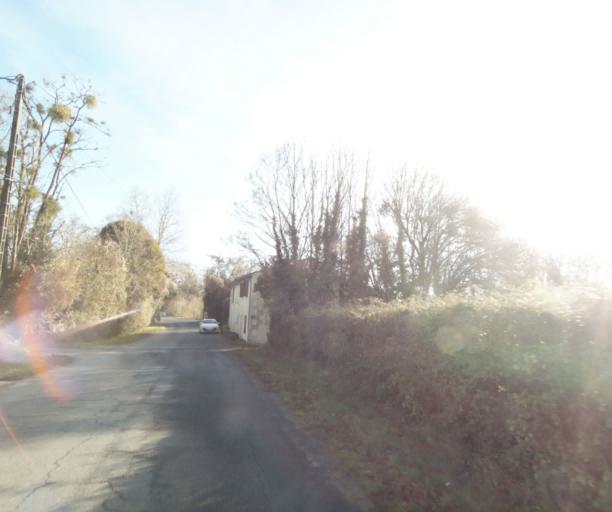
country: FR
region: Poitou-Charentes
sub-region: Departement de la Charente-Maritime
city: Chaniers
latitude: 45.7132
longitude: -0.5469
